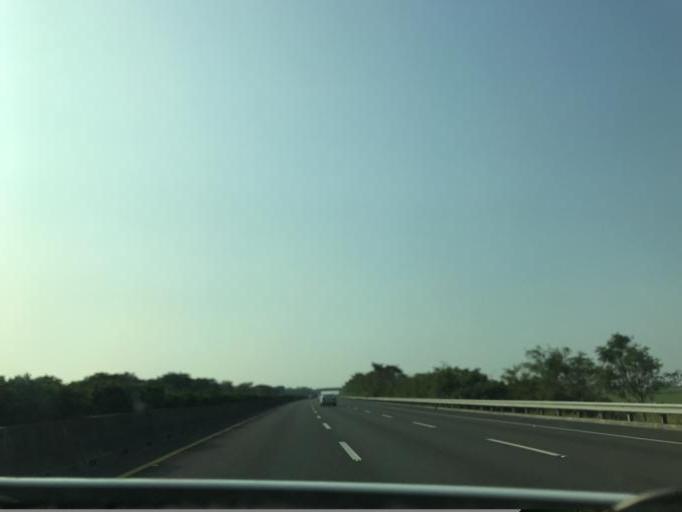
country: TW
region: Taiwan
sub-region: Chiayi
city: Taibao
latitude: 23.3891
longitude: 120.3554
